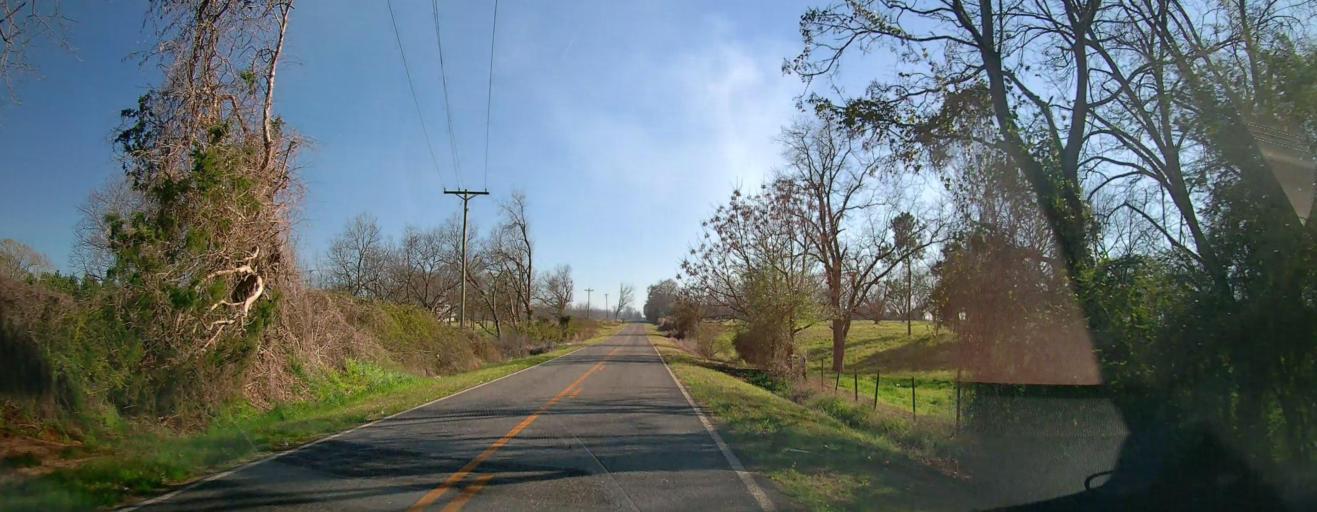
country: US
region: Georgia
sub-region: Peach County
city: Fort Valley
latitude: 32.6143
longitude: -83.8521
